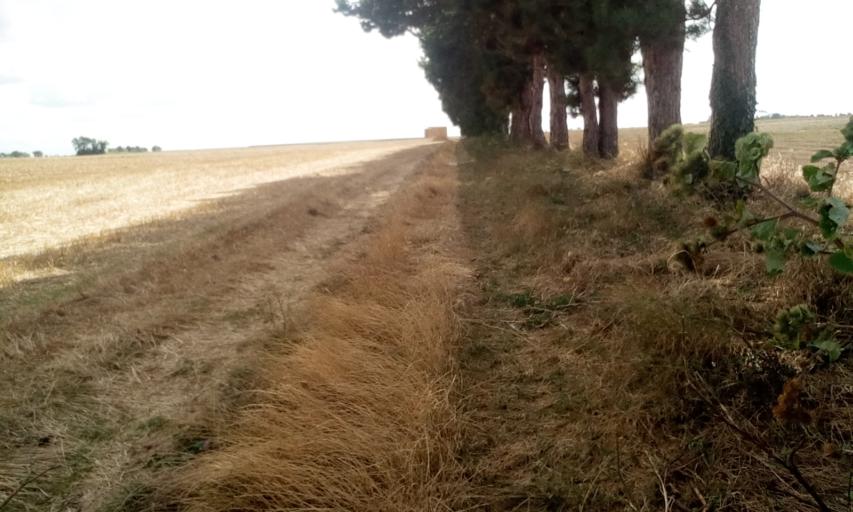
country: FR
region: Lower Normandy
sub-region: Departement du Calvados
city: Bellengreville
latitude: 49.0918
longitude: -0.2042
